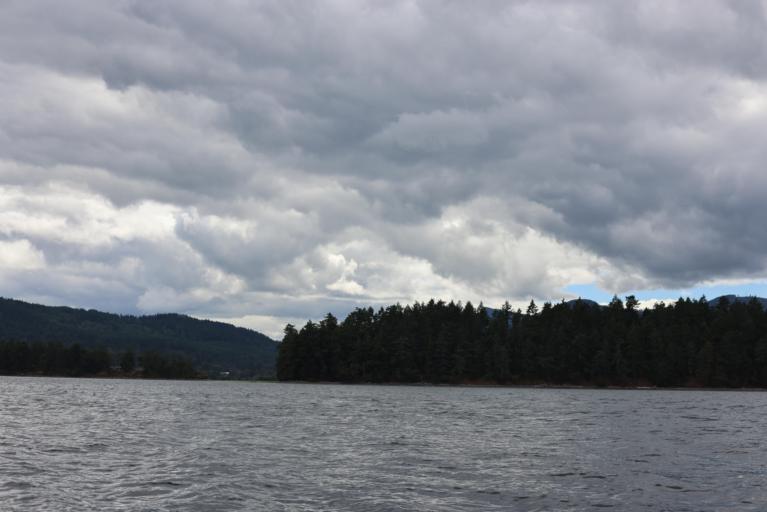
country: CA
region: British Columbia
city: North Cowichan
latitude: 48.8999
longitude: -123.6522
